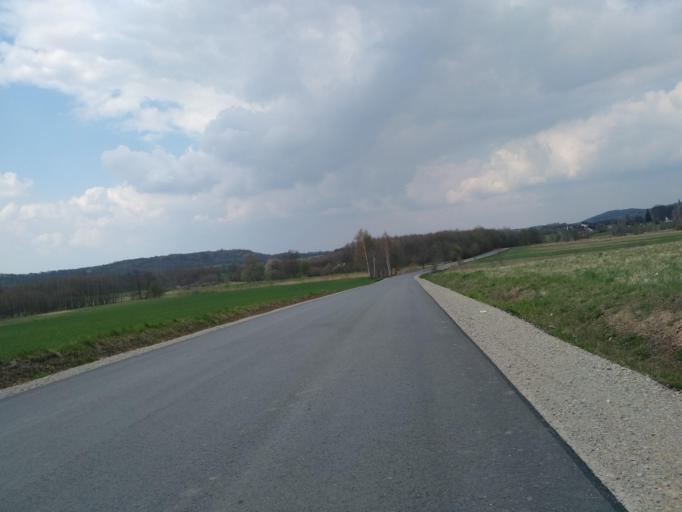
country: PL
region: Subcarpathian Voivodeship
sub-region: Powiat sanocki
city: Strachocina
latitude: 49.5919
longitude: 22.1034
